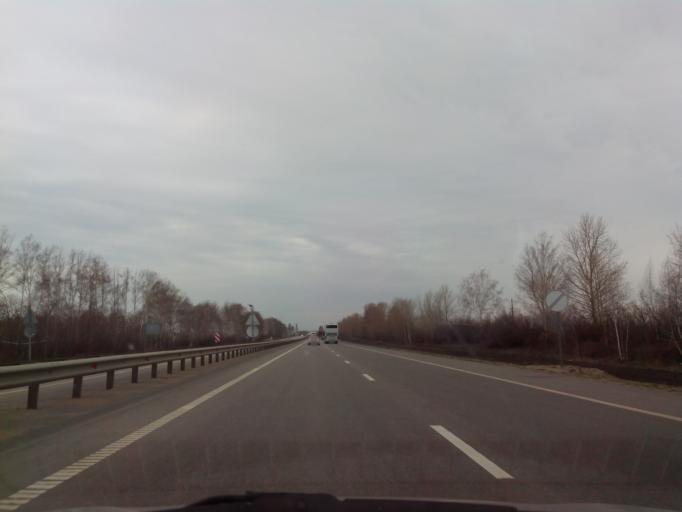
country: RU
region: Tambov
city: Selezni
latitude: 52.8082
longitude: 40.9622
